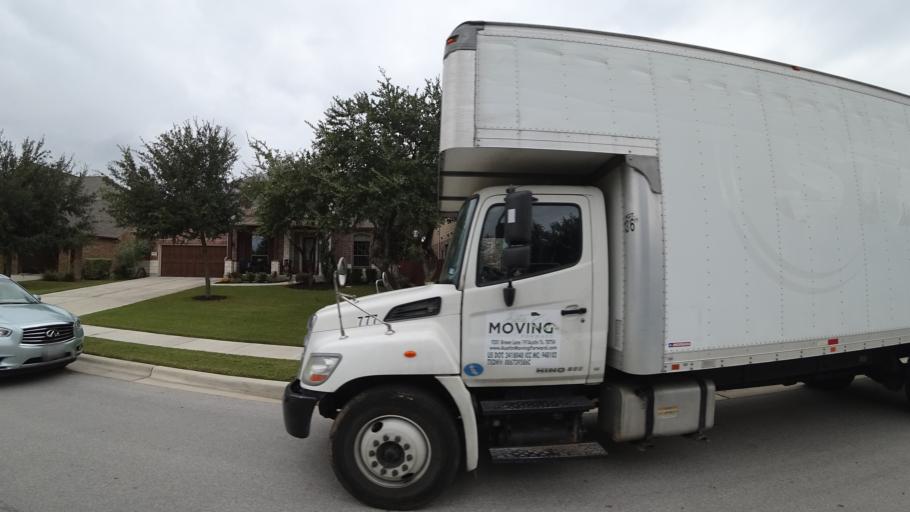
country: US
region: Texas
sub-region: Travis County
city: Bee Cave
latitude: 30.3410
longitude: -97.9031
